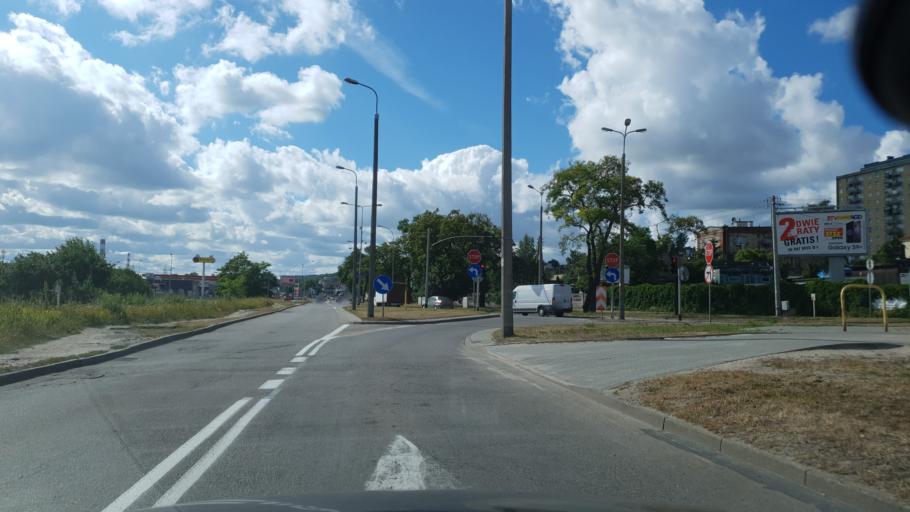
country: PL
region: Pomeranian Voivodeship
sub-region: Gdynia
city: Gdynia
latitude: 54.5482
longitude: 18.5173
